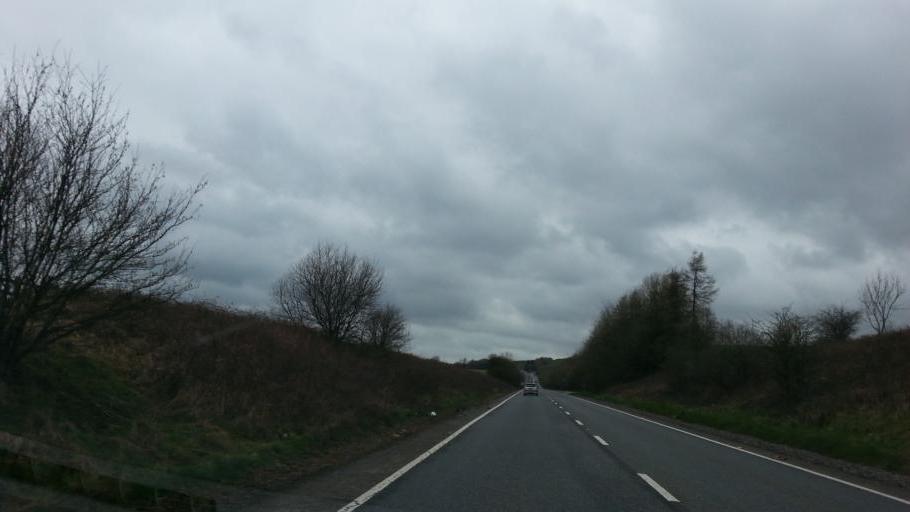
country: GB
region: England
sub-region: Devon
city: South Molton
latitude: 51.0341
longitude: -3.8442
